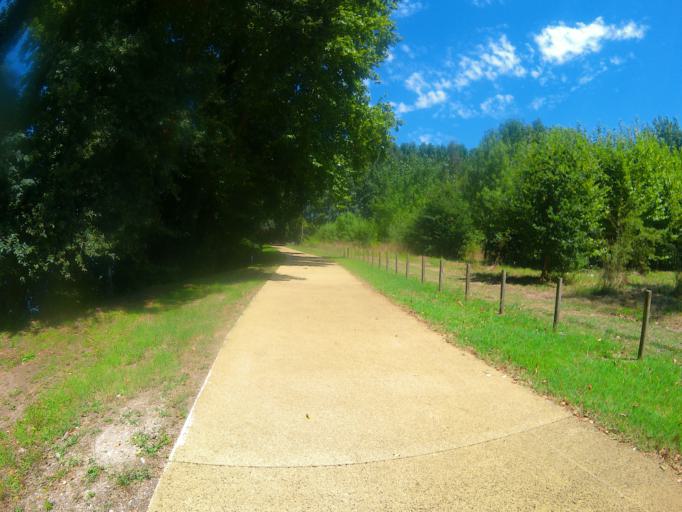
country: PT
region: Viana do Castelo
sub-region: Valenca
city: Valenca
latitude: 41.9864
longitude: -8.6909
